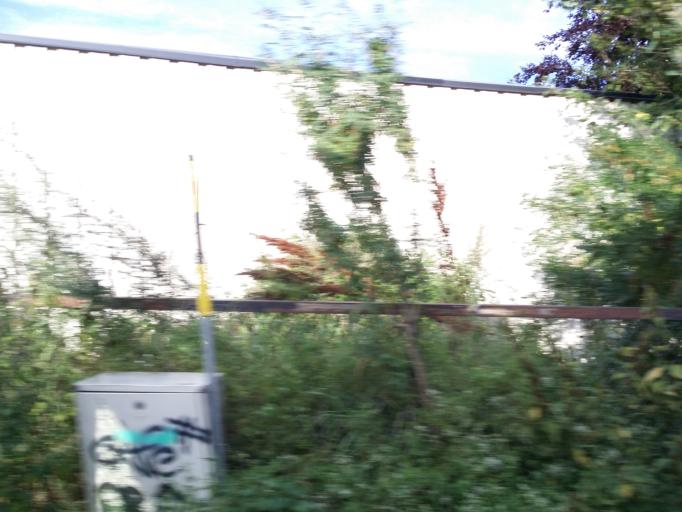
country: NO
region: Oslo
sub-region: Oslo
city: Oslo
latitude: 59.9102
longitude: 10.8494
